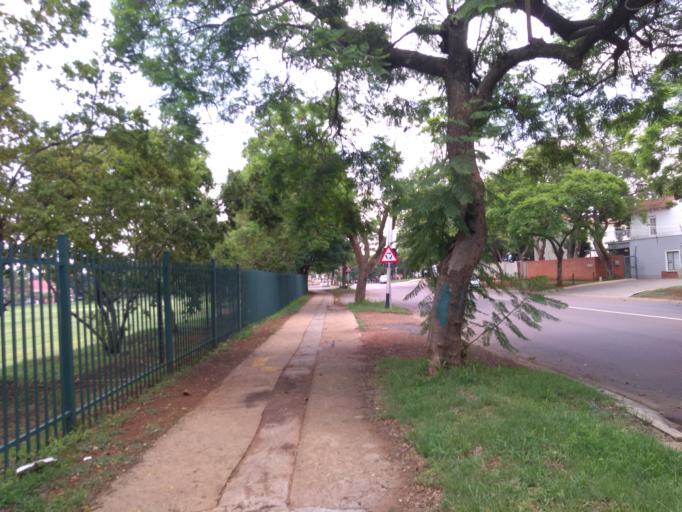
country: ZA
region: Gauteng
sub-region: City of Tshwane Metropolitan Municipality
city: Pretoria
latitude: -25.7604
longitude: 28.2303
